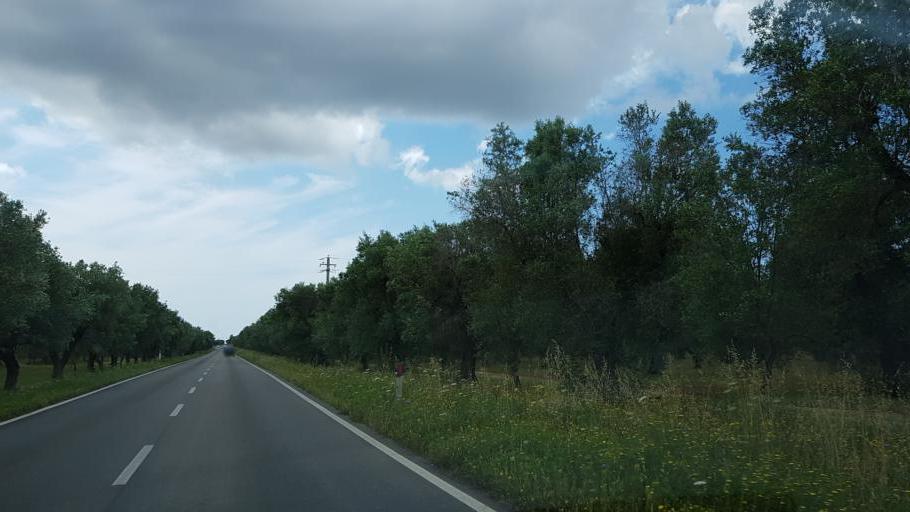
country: IT
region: Apulia
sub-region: Provincia di Brindisi
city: San Pancrazio Salentino
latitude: 40.3611
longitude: 17.8425
